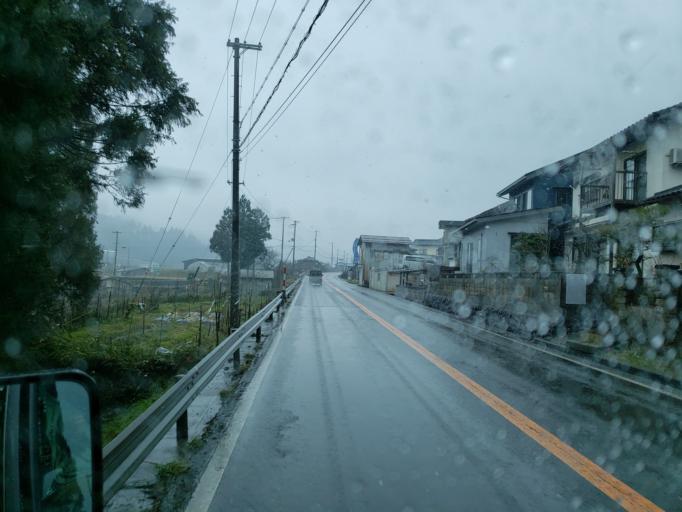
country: JP
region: Hyogo
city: Toyooka
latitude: 35.3848
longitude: 134.7068
